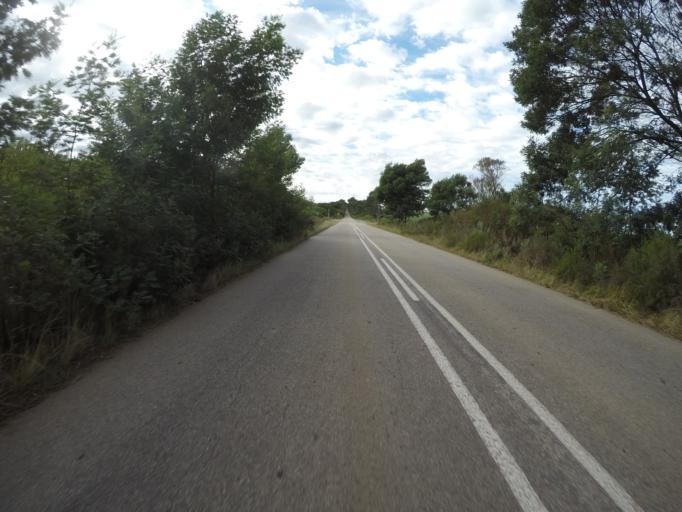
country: ZA
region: Eastern Cape
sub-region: Cacadu District Municipality
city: Kareedouw
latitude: -34.0463
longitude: 24.4571
